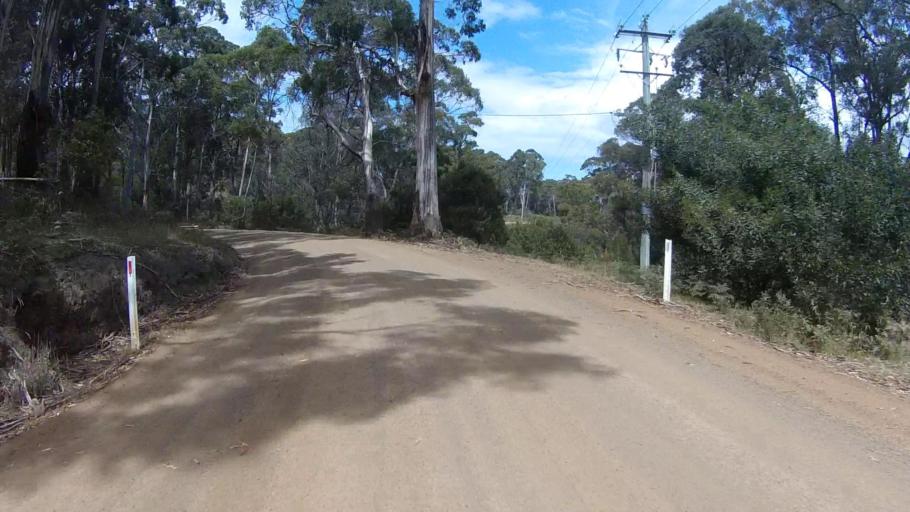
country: AU
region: Tasmania
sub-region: Kingborough
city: Blackmans Bay
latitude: -43.0453
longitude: 147.3066
